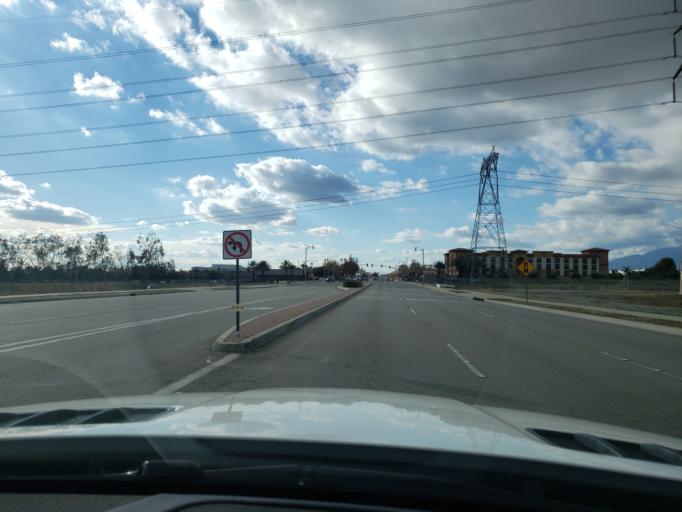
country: US
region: California
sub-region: San Bernardino County
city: Rancho Cucamonga
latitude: 34.1064
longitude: -117.5399
